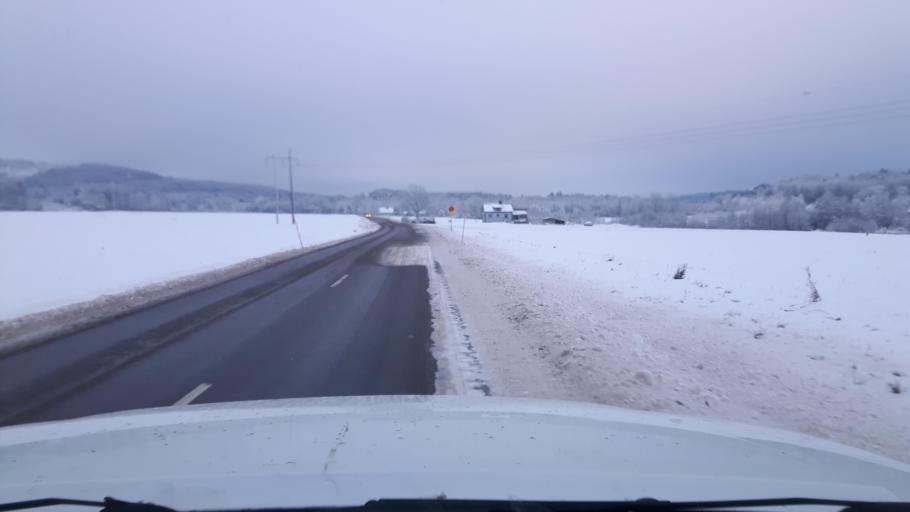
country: SE
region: Halland
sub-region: Kungsbacka Kommun
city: Fjaeras kyrkby
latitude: 57.4228
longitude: 12.1993
